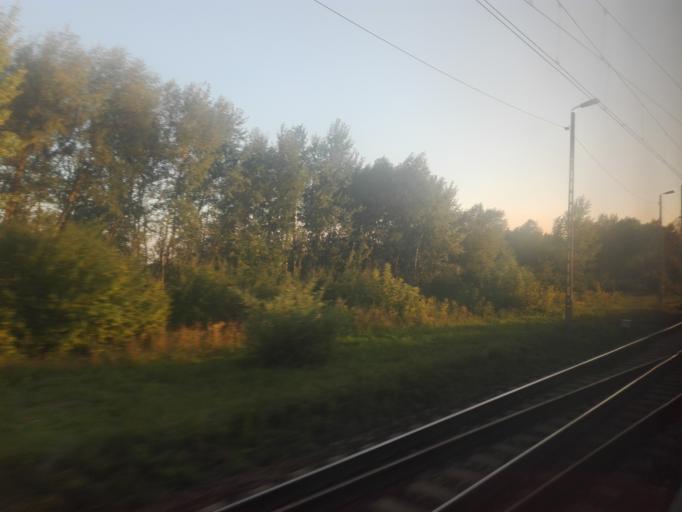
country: PL
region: Masovian Voivodeship
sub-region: Powiat warszawski zachodni
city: Blonie
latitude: 52.1864
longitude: 20.5918
